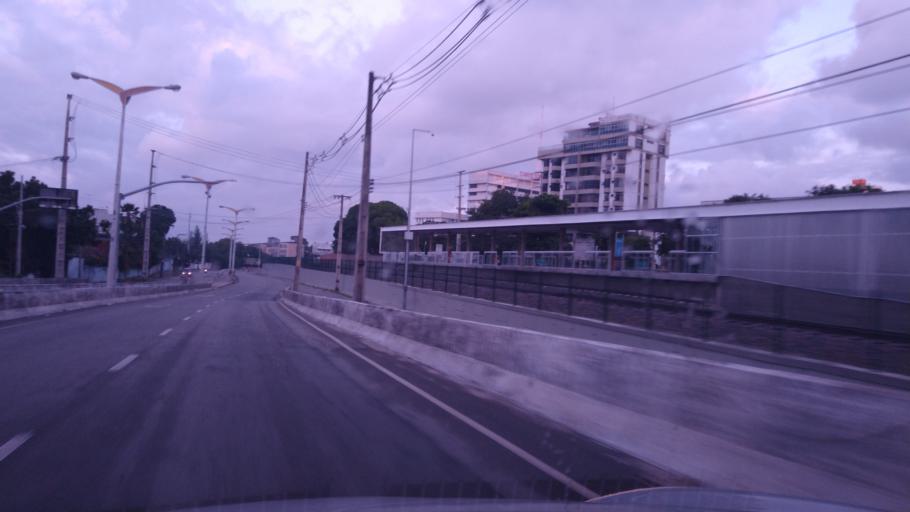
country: BR
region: Ceara
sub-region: Fortaleza
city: Fortaleza
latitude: -3.7487
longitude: -38.4932
